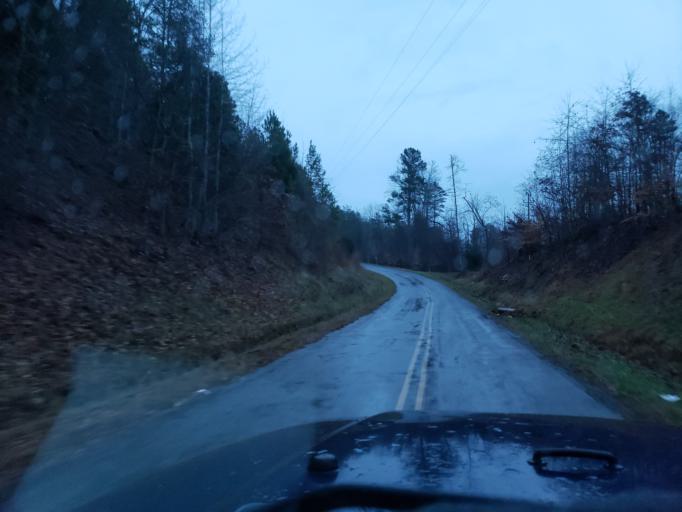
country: US
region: North Carolina
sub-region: Cleveland County
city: White Plains
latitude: 35.1454
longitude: -81.4090
